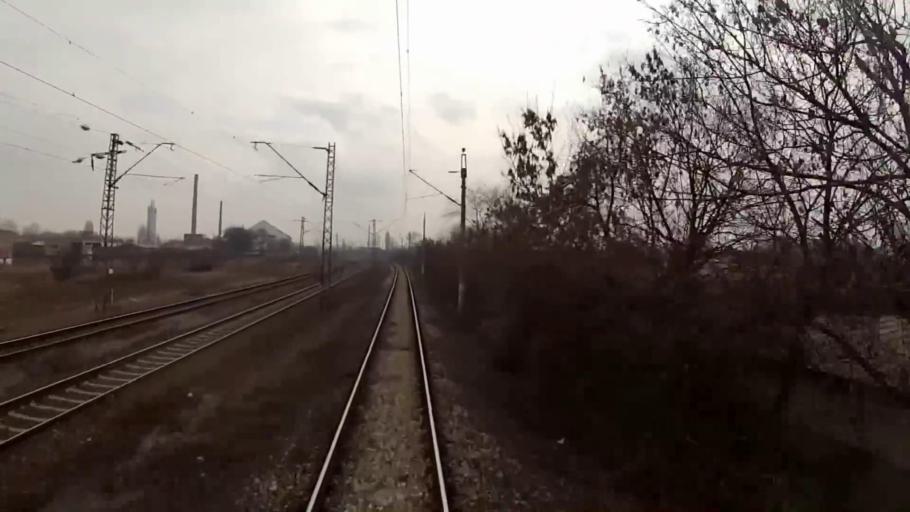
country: BG
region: Sofia-Capital
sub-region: Stolichna Obshtina
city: Sofia
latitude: 42.6605
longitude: 23.4318
